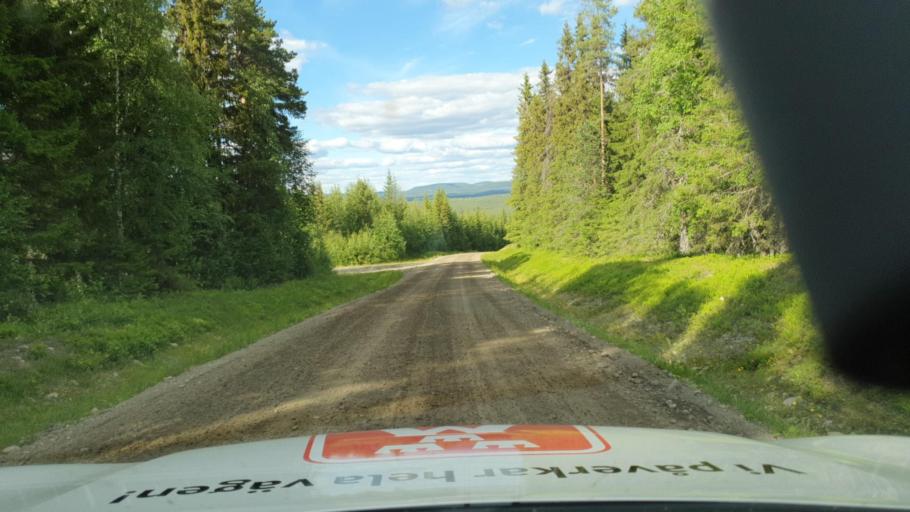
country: SE
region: Vaesterbotten
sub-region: Lycksele Kommun
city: Lycksele
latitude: 64.3616
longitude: 18.5407
